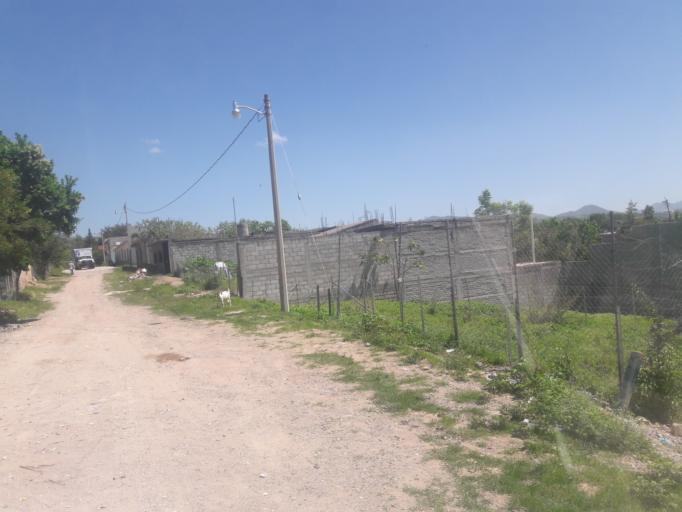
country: MX
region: Oaxaca
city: Ciudad de Huajuapam de Leon
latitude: 17.8019
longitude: -97.8010
